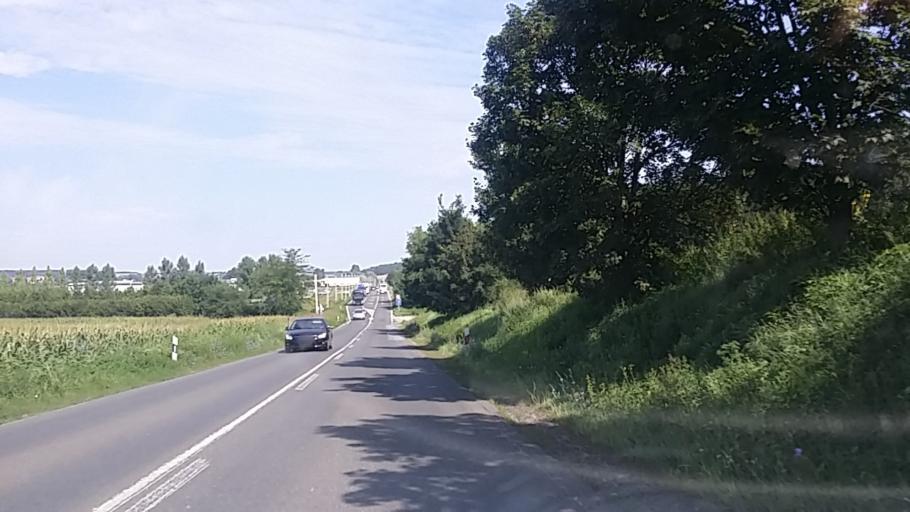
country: HU
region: Baranya
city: Sasd
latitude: 46.2362
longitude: 18.1212
